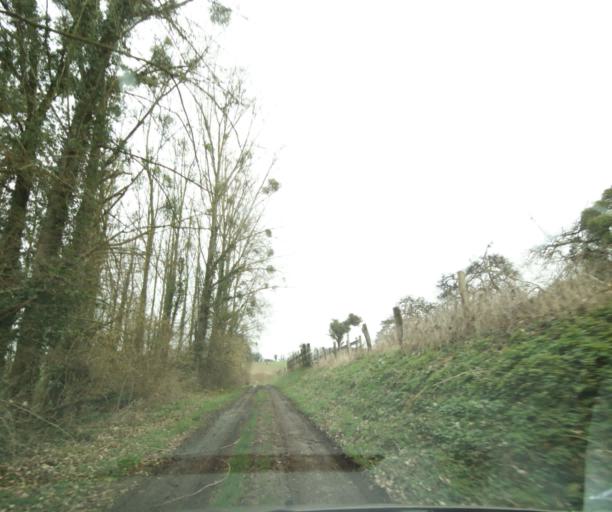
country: FR
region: Picardie
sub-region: Departement de l'Oise
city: Crisolles
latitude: 49.6030
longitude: 3.0197
